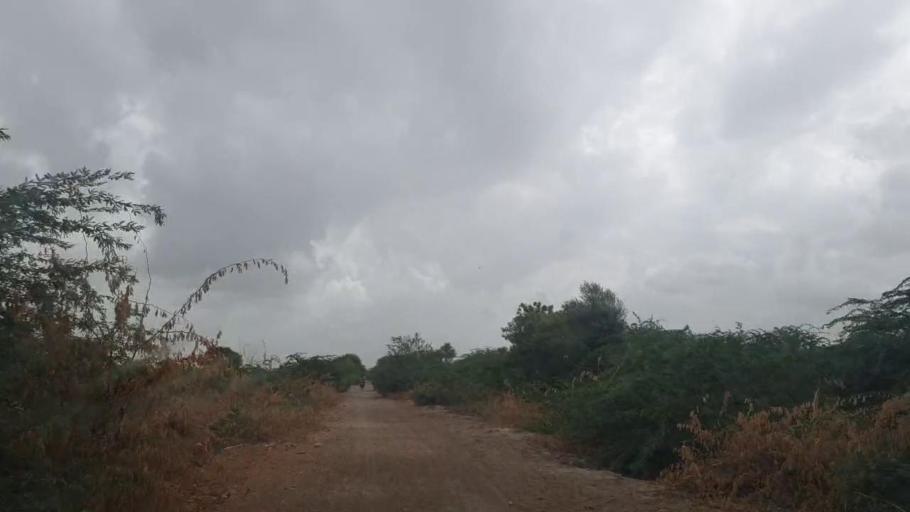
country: PK
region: Sindh
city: Naukot
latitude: 24.8657
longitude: 69.2225
